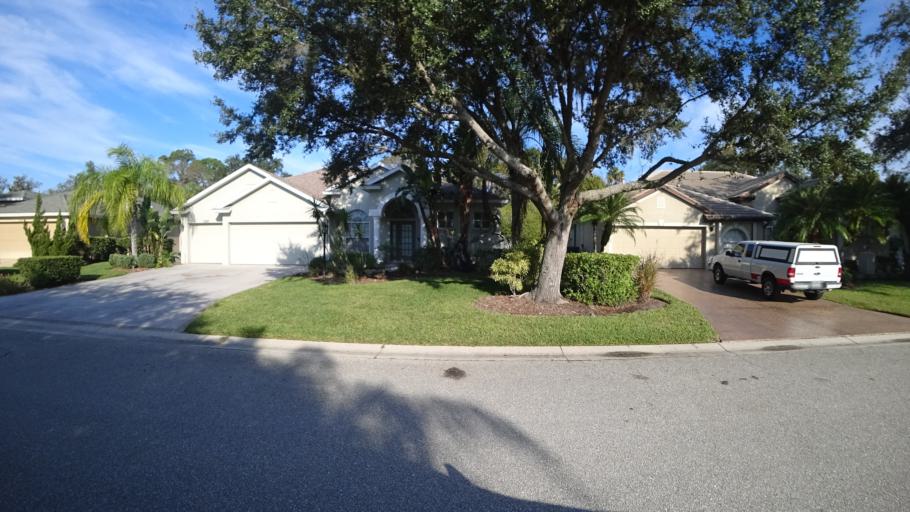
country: US
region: Florida
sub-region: Sarasota County
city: Desoto Lakes
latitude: 27.4239
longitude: -82.4972
